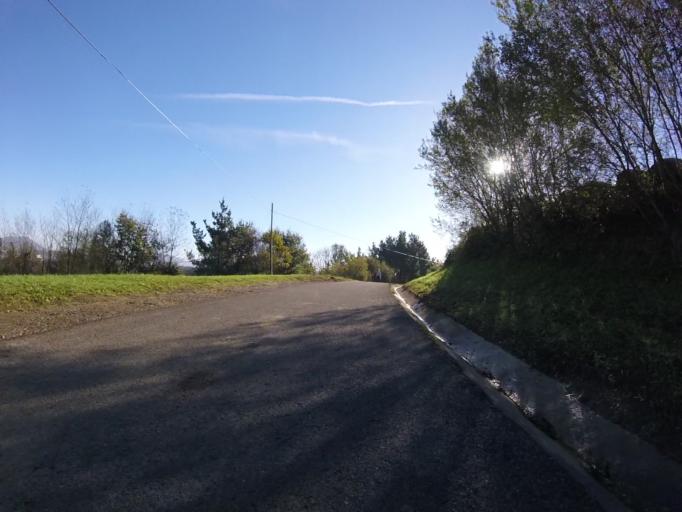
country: ES
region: Basque Country
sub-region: Provincia de Guipuzcoa
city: Usurbil
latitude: 43.2937
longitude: -2.0392
